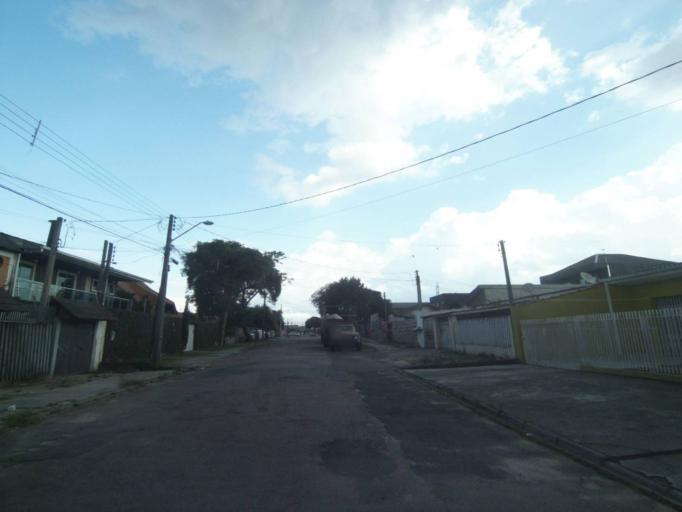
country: BR
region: Parana
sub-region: Sao Jose Dos Pinhais
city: Sao Jose dos Pinhais
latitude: -25.5333
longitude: -49.2723
